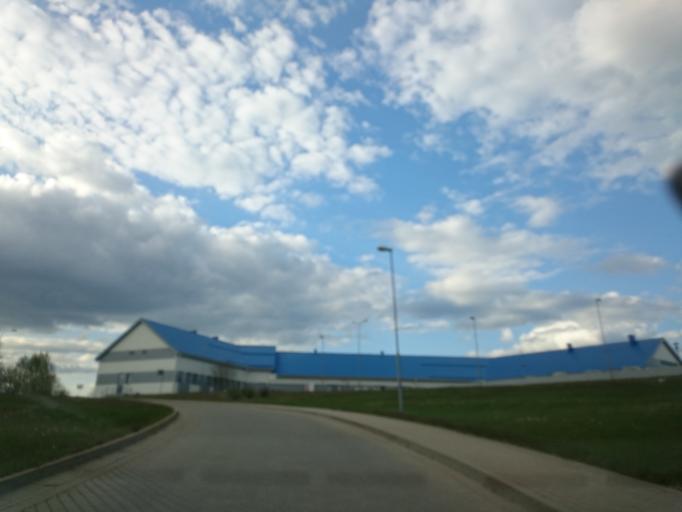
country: LV
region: Kuldigas Rajons
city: Kuldiga
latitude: 56.9612
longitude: 21.9541
